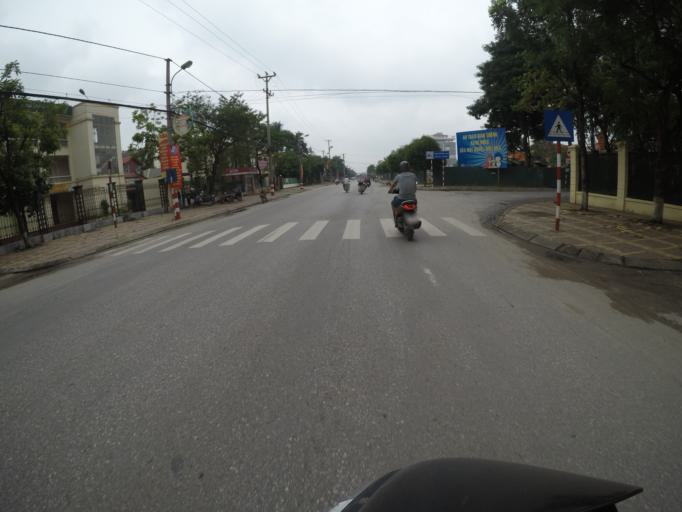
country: VN
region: Ha Noi
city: Soc Son
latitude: 21.2587
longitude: 105.8487
